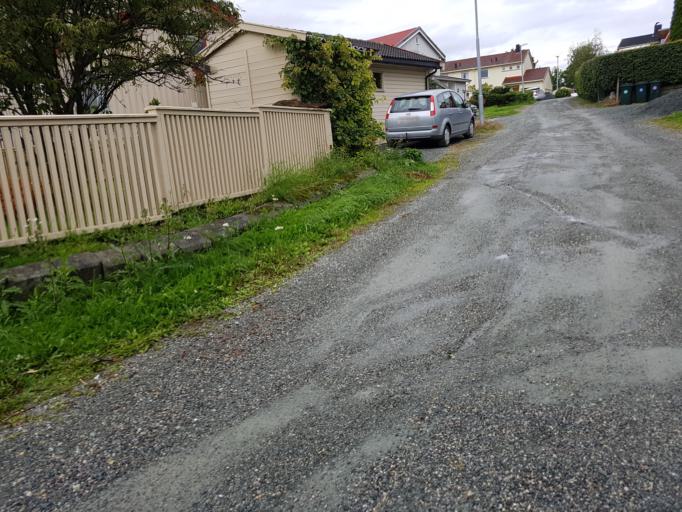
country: NO
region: Sor-Trondelag
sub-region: Trondheim
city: Trondheim
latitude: 63.3924
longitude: 10.4203
